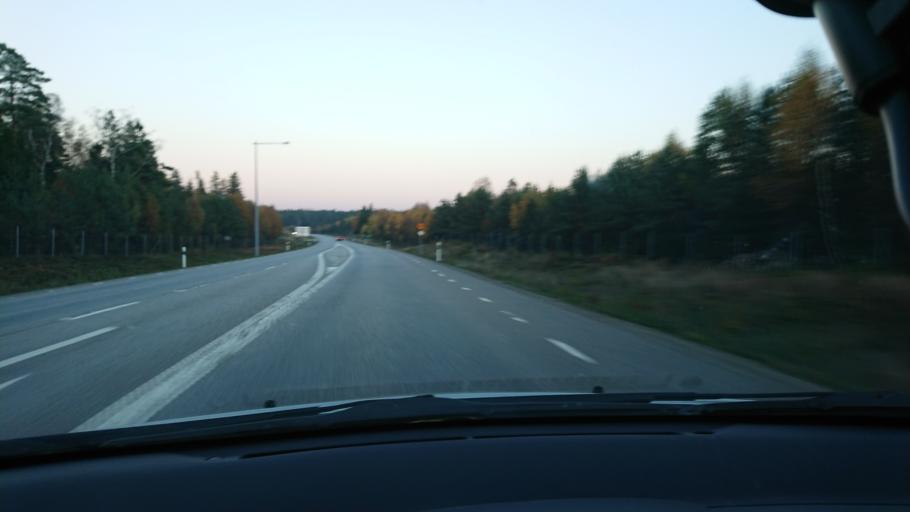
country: SE
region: Halland
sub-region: Laholms Kommun
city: Knared
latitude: 56.7395
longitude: 13.4612
